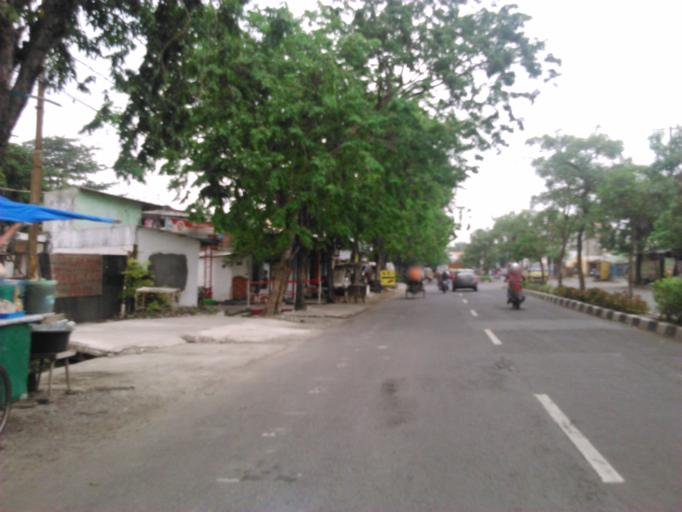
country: ID
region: East Java
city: Gubengairlangga
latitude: -7.2734
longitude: 112.7619
